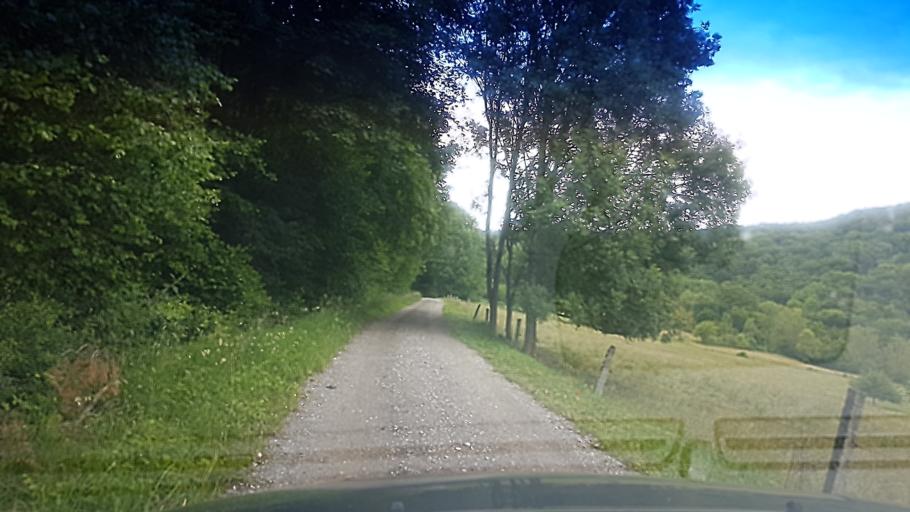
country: DE
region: Bavaria
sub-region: Upper Franconia
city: Buttenheim
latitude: 49.8321
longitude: 11.0529
